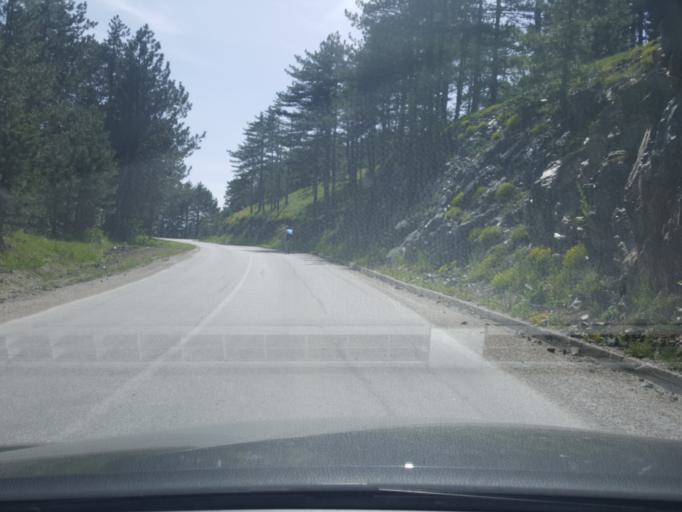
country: RS
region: Central Serbia
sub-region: Zlatiborski Okrug
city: Bajina Basta
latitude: 43.8787
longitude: 19.5657
